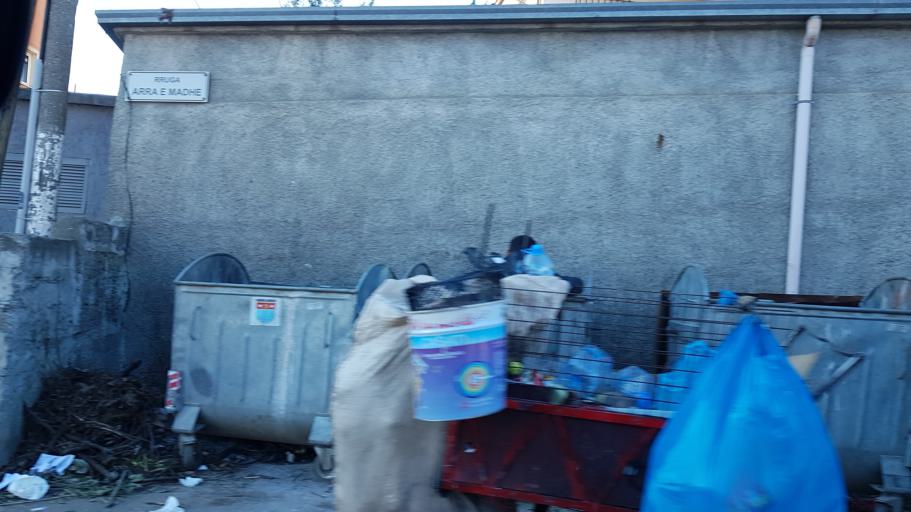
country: AL
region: Shkoder
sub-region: Rrethi i Shkodres
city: Shkoder
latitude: 42.0606
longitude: 19.5172
